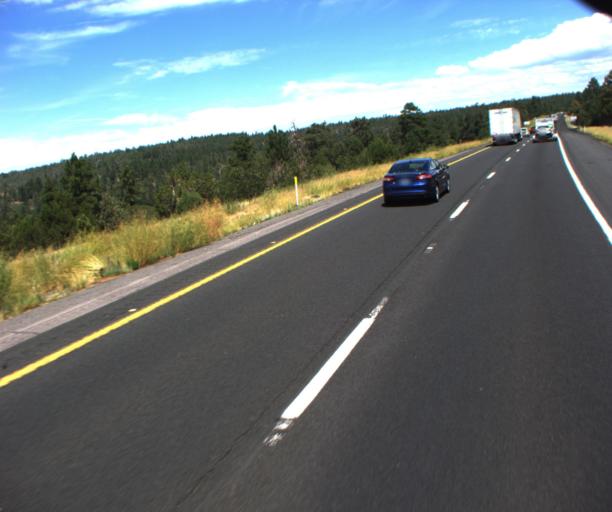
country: US
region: Arizona
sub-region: Yavapai County
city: Village of Oak Creek (Big Park)
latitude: 34.8149
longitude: -111.6110
